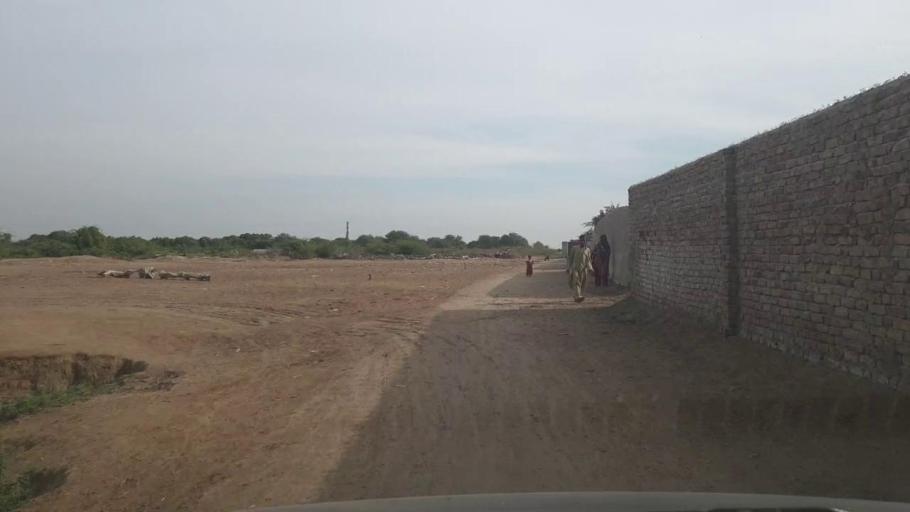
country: PK
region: Sindh
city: Kunri
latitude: 25.2953
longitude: 69.5894
